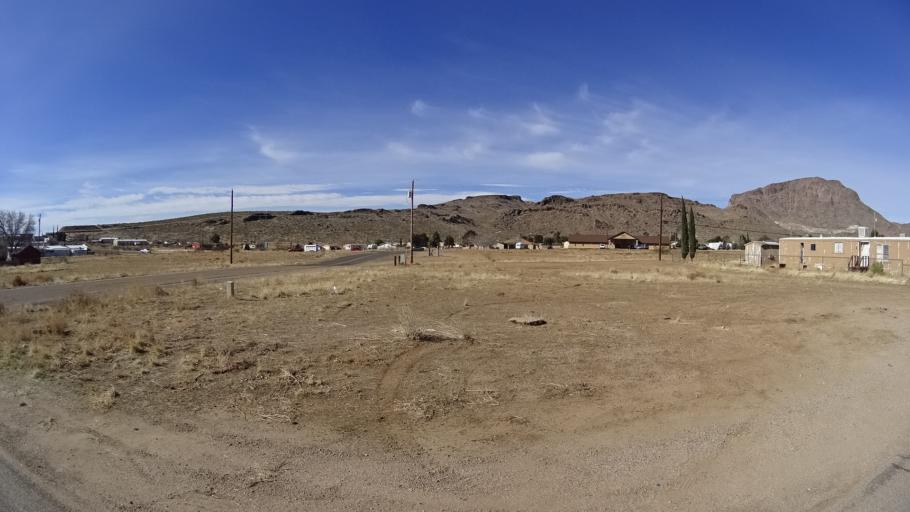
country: US
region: Arizona
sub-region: Mohave County
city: New Kingman-Butler
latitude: 35.2605
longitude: -114.0375
